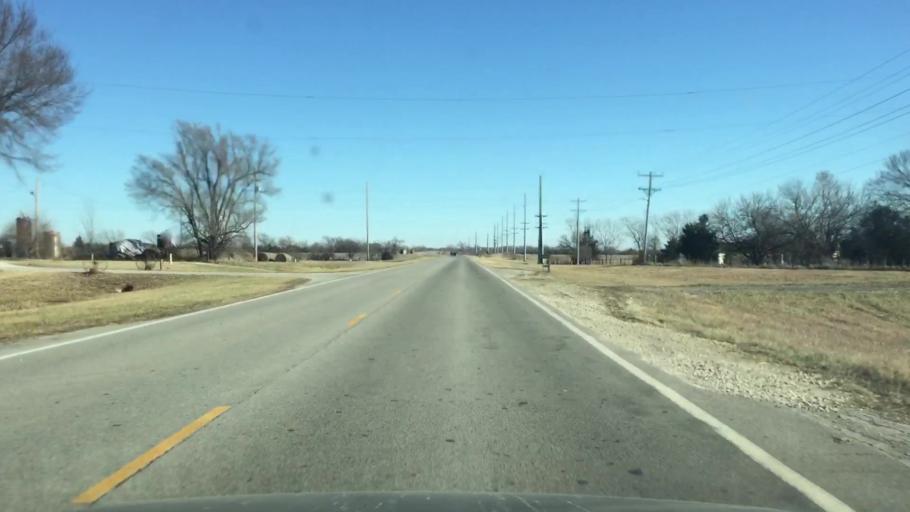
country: US
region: Kansas
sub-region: Allen County
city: Humboldt
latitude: 37.8201
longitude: -95.4220
